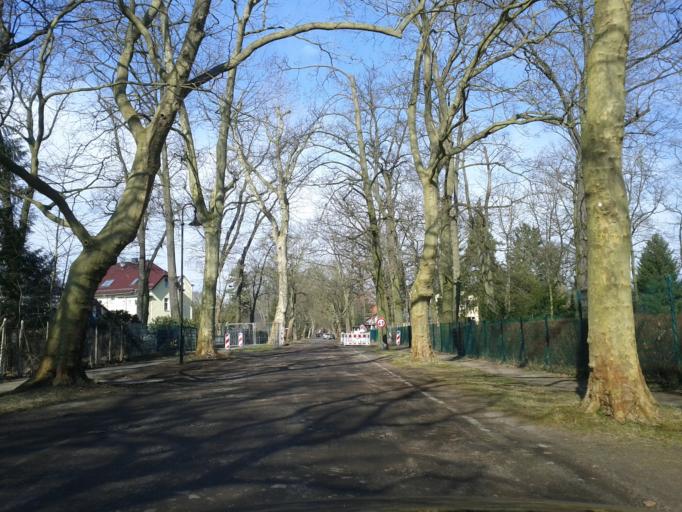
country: DE
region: Brandenburg
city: Schoneiche
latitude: 52.4685
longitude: 13.6933
